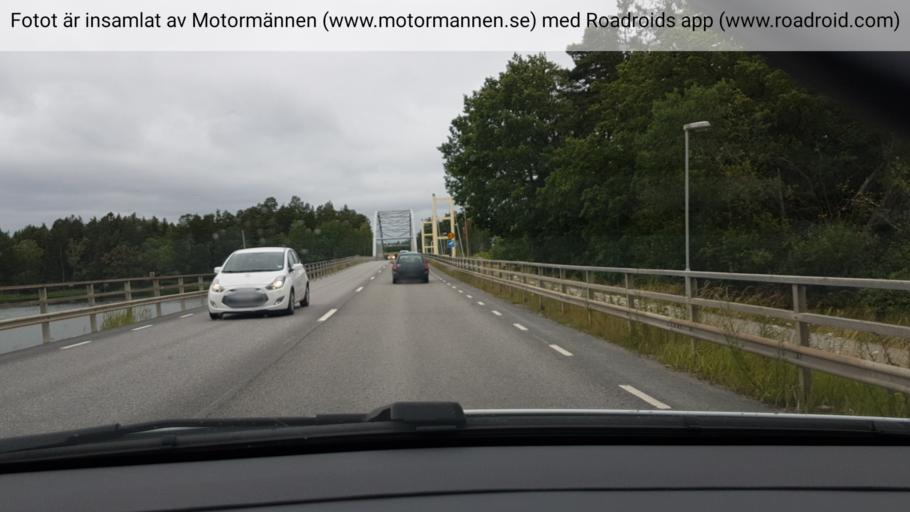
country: SE
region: Stockholm
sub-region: Vaxholms Kommun
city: Resaro
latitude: 59.4081
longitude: 18.3168
